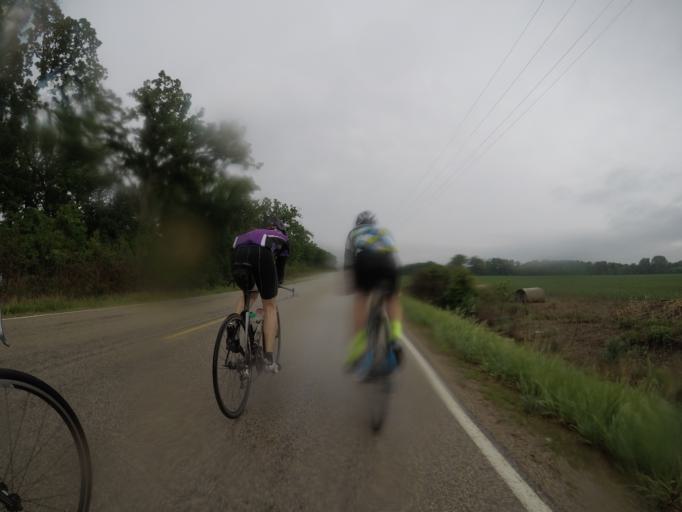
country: US
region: Kansas
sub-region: Pottawatomie County
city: Wamego
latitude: 39.3368
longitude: -96.2213
